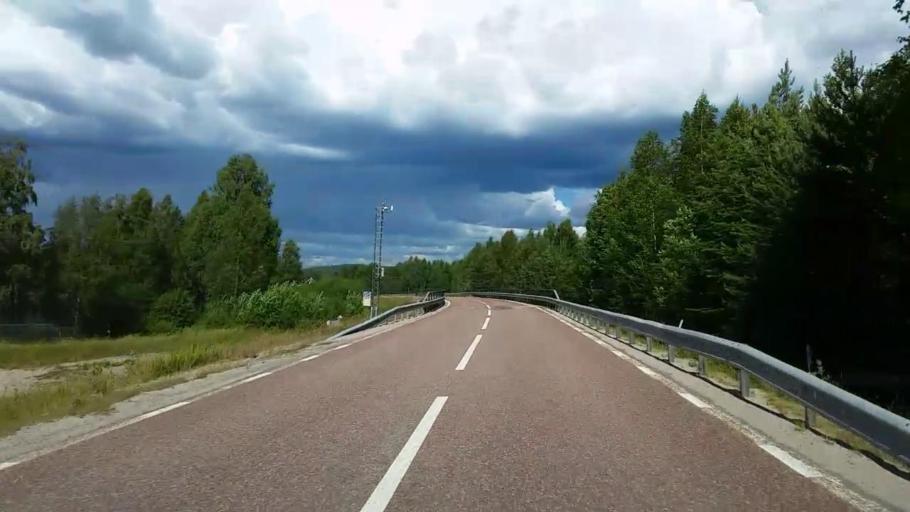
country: SE
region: Gaevleborg
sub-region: Ovanakers Kommun
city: Edsbyn
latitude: 61.3352
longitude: 15.5421
